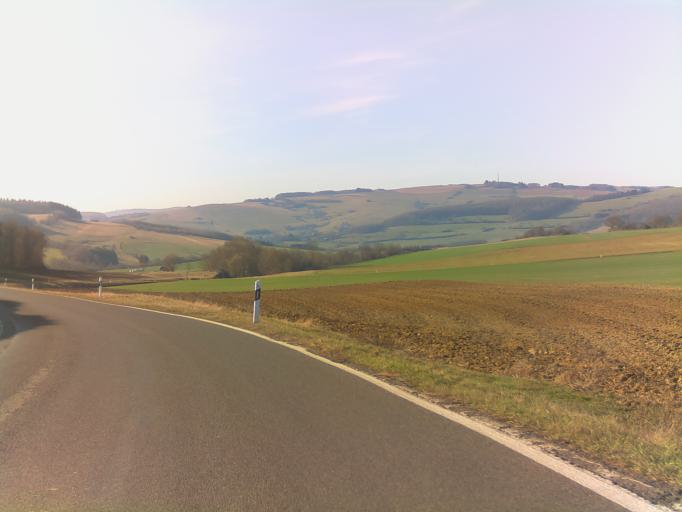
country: DE
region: Rheinland-Pfalz
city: Gerbach
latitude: 49.6698
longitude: 7.8447
